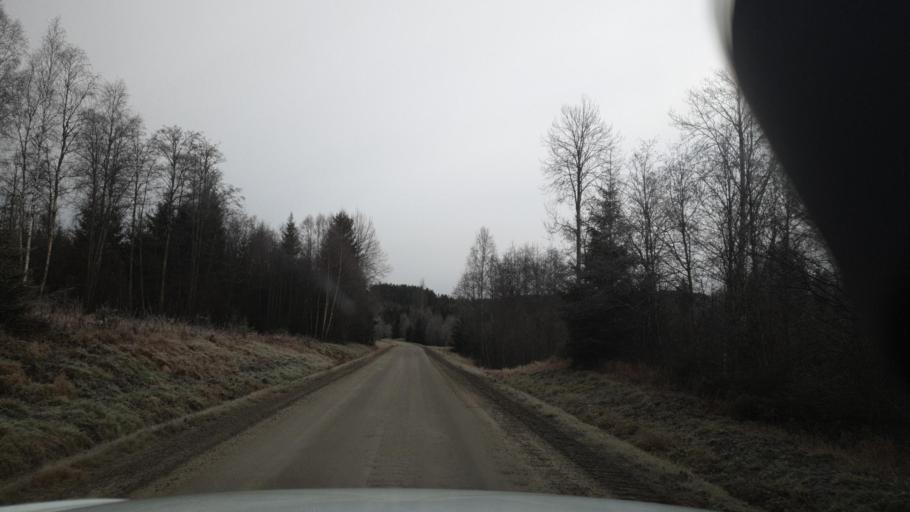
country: SE
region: Vaermland
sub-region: Arvika Kommun
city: Arvika
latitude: 59.8338
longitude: 12.7472
